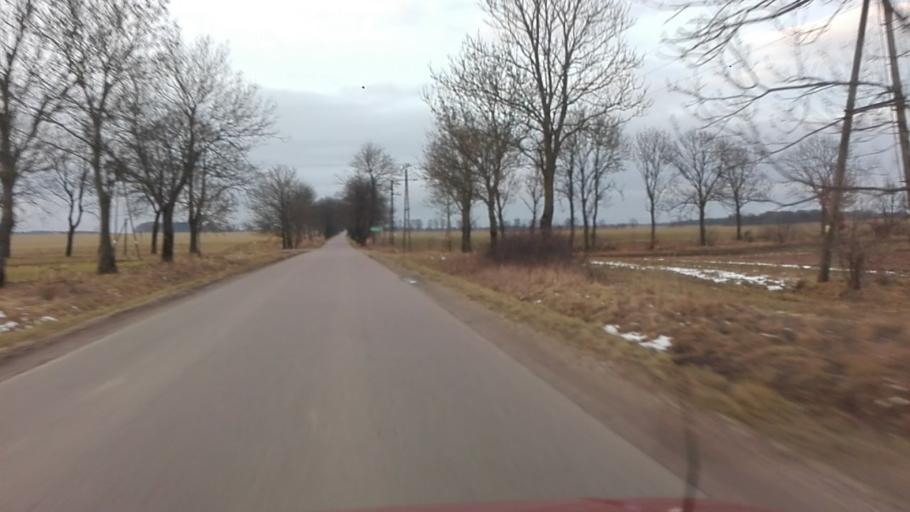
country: PL
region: West Pomeranian Voivodeship
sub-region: Powiat swidwinski
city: Rabino
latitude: 53.8056
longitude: 15.9143
